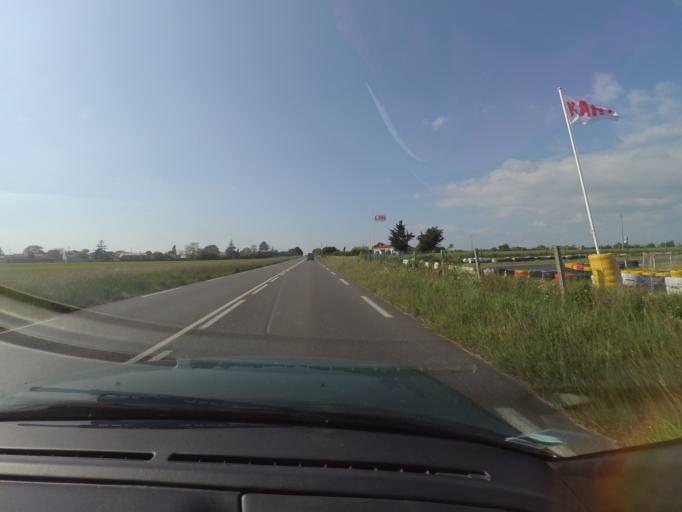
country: FR
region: Pays de la Loire
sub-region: Departement de la Vendee
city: Angles
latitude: 46.4219
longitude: -1.3928
